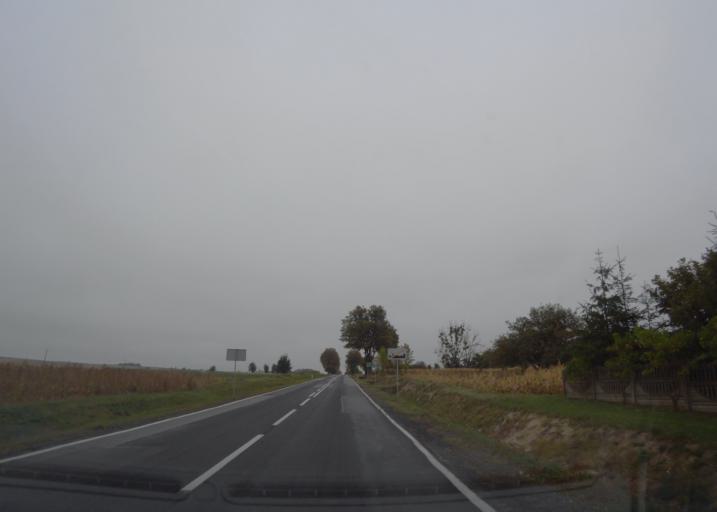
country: PL
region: Lublin Voivodeship
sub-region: Powiat chelmski
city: Rejowiec
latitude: 51.0358
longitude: 23.2451
